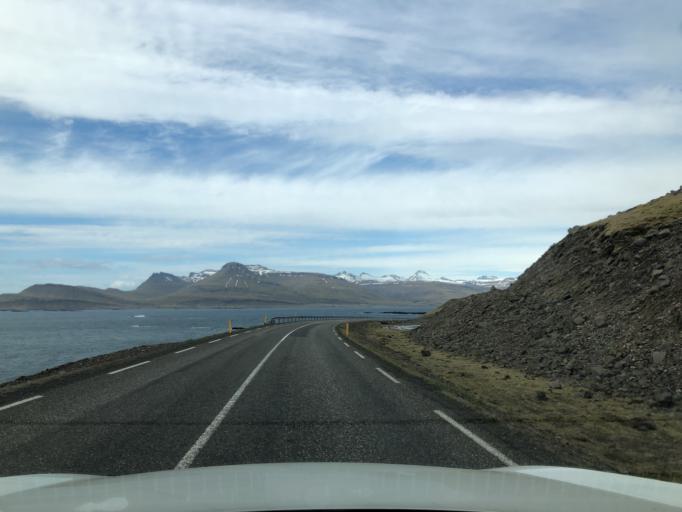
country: IS
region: East
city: Eskifjoerdur
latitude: 64.7953
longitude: -13.9240
